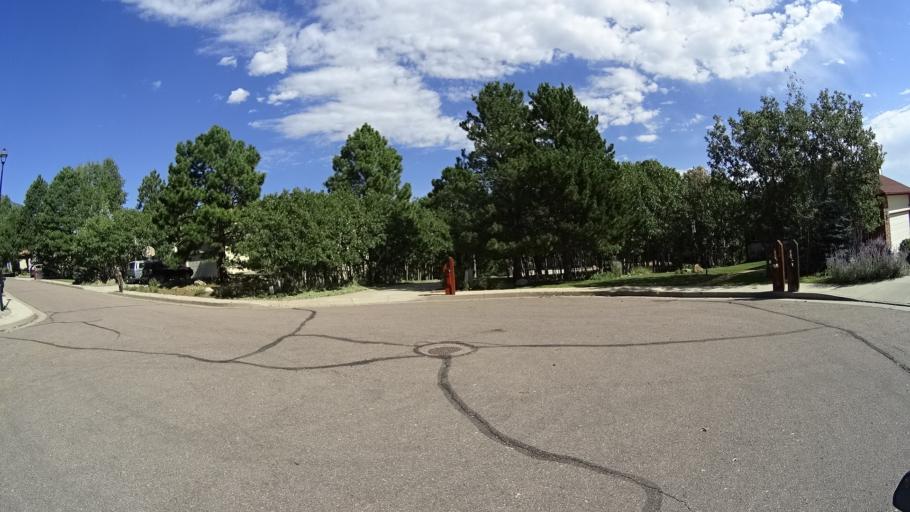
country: US
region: Colorado
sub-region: El Paso County
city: Fort Carson
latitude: 38.7627
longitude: -104.8264
